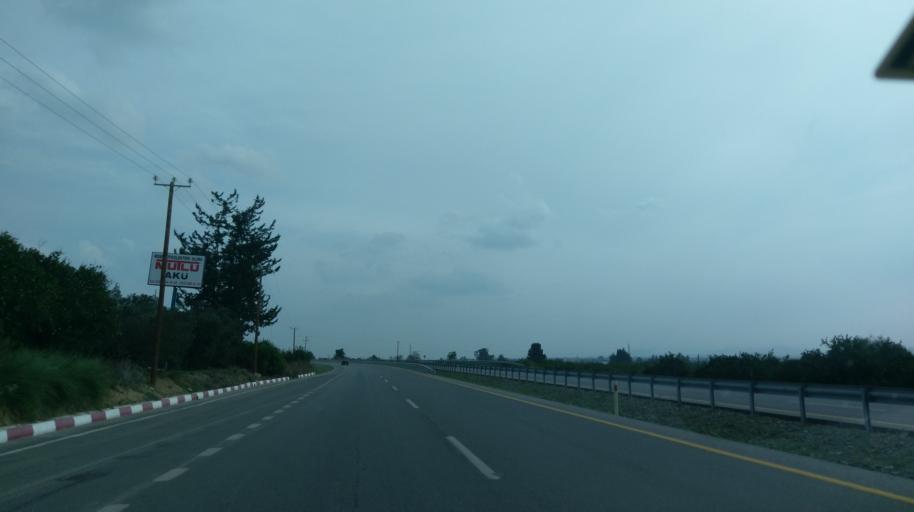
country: CY
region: Lefkosia
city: Morfou
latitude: 35.1993
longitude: 33.0509
